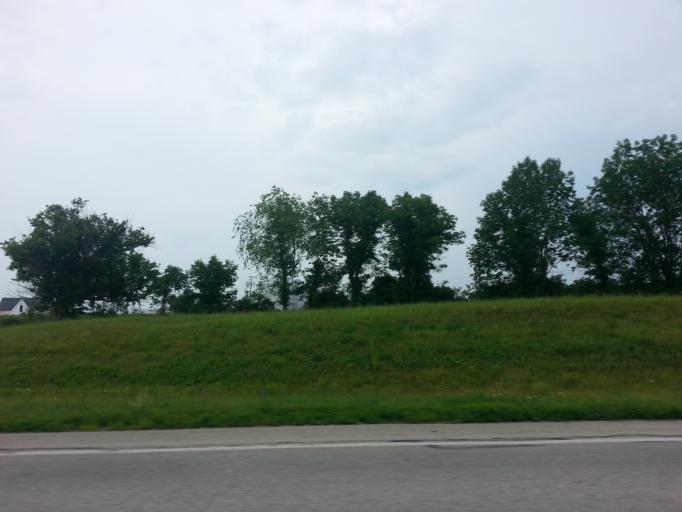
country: US
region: Ohio
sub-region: Brown County
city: Georgetown
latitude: 38.8306
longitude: -83.8329
